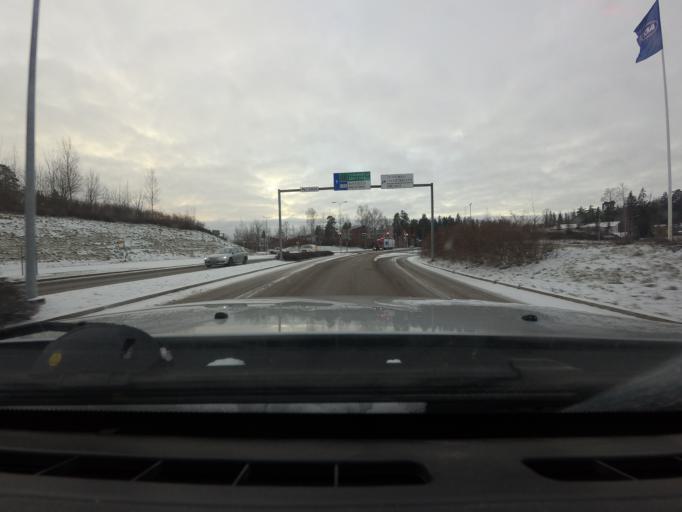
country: FI
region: Uusimaa
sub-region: Helsinki
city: Kilo
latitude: 60.2125
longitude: 24.7636
